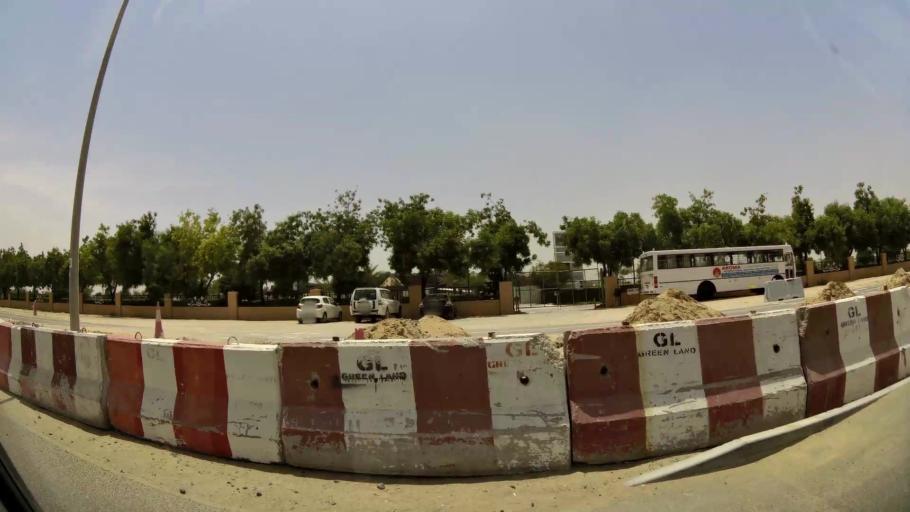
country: AE
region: Ash Shariqah
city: Sharjah
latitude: 25.2389
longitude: 55.4772
